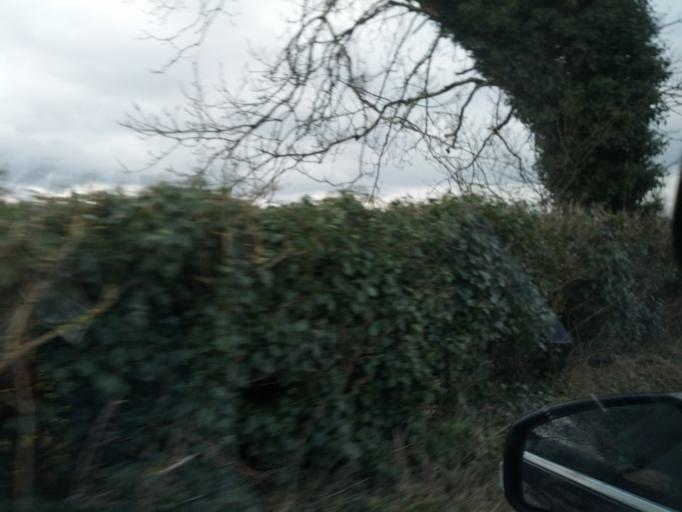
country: IE
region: Connaught
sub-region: County Galway
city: Athenry
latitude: 53.4963
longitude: -8.6004
